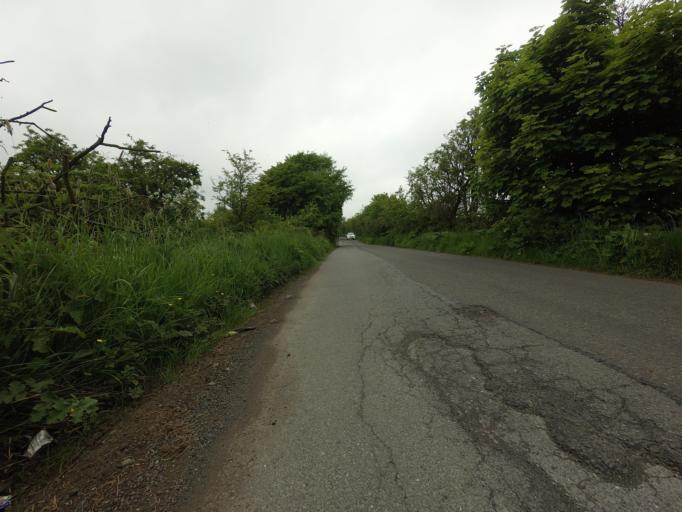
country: GB
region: Scotland
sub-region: Fife
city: Townhill
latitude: 56.1249
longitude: -3.4361
